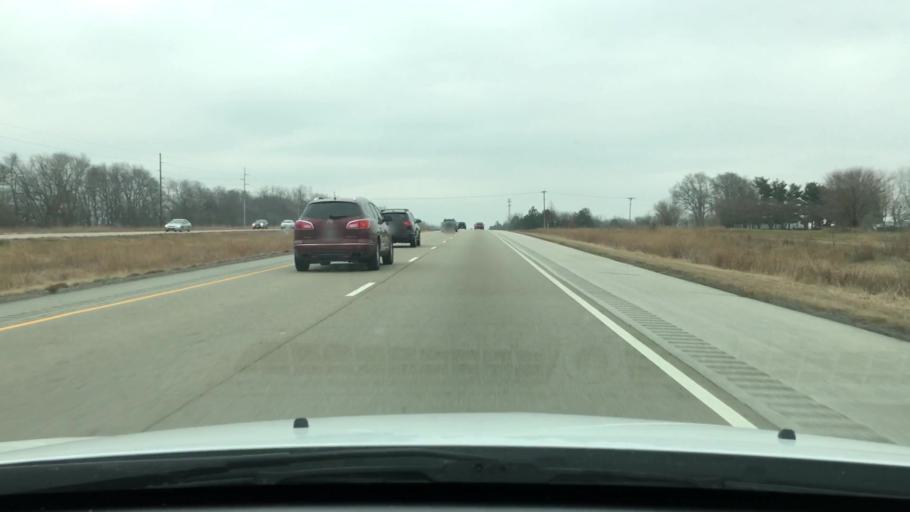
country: US
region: Illinois
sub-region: Logan County
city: Atlanta
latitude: 40.2358
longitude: -89.2600
